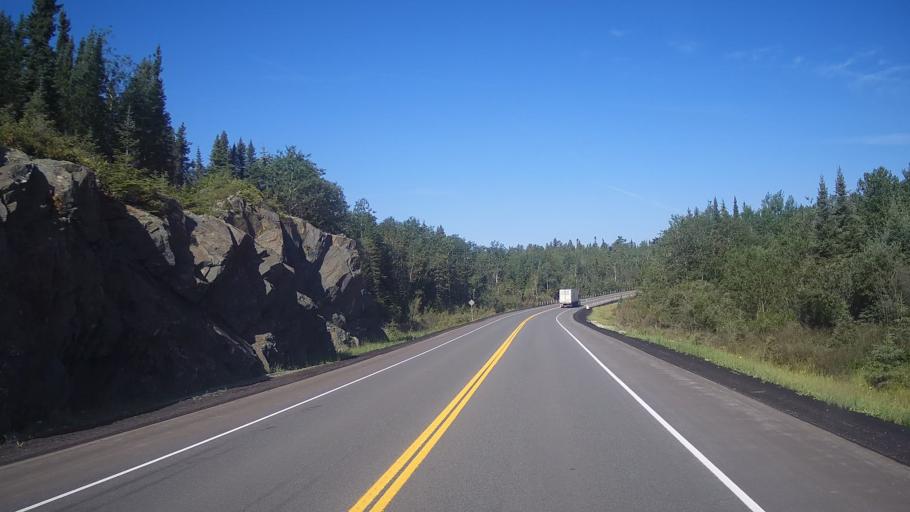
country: CA
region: Ontario
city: Dryden
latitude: 49.6476
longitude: -92.4617
